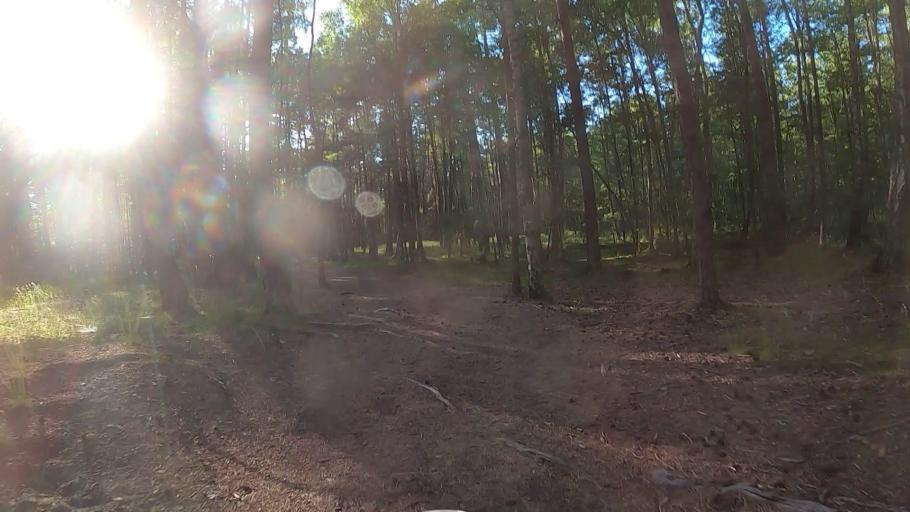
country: LV
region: Carnikava
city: Carnikava
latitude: 57.1385
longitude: 24.2433
